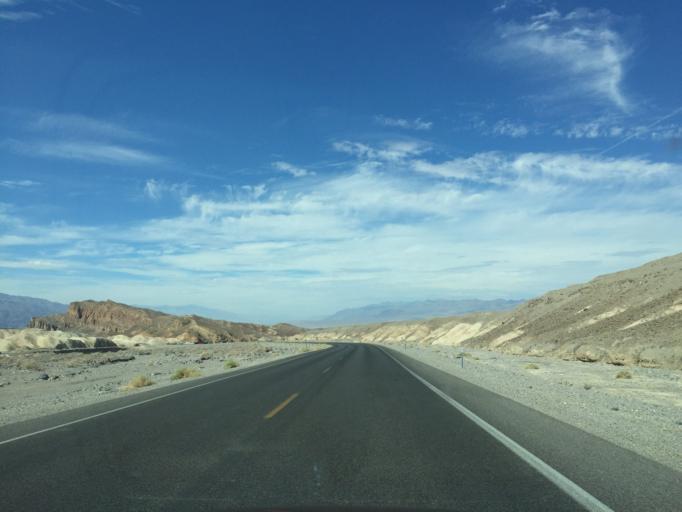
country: US
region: Nevada
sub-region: Nye County
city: Beatty
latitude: 36.4169
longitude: -116.8045
